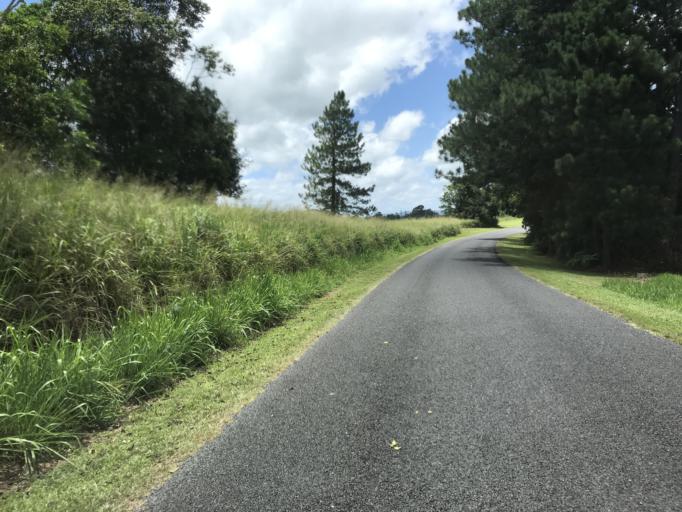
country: AU
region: Queensland
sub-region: Tablelands
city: Atherton
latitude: -17.3385
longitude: 145.5808
